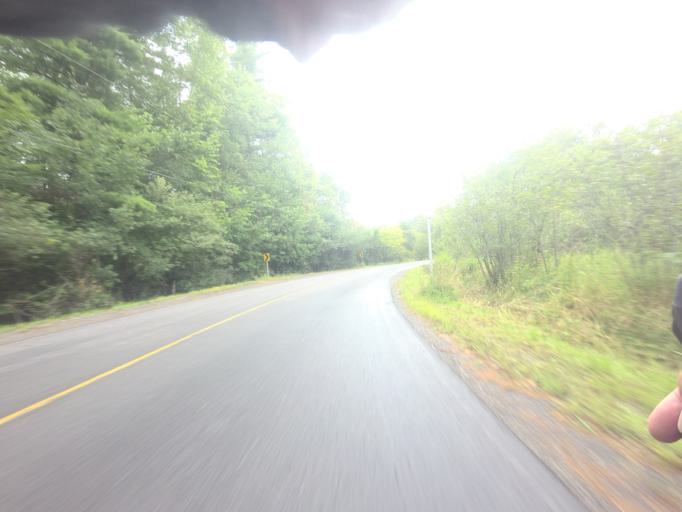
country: CA
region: Ontario
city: Bells Corners
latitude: 45.3448
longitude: -75.9658
